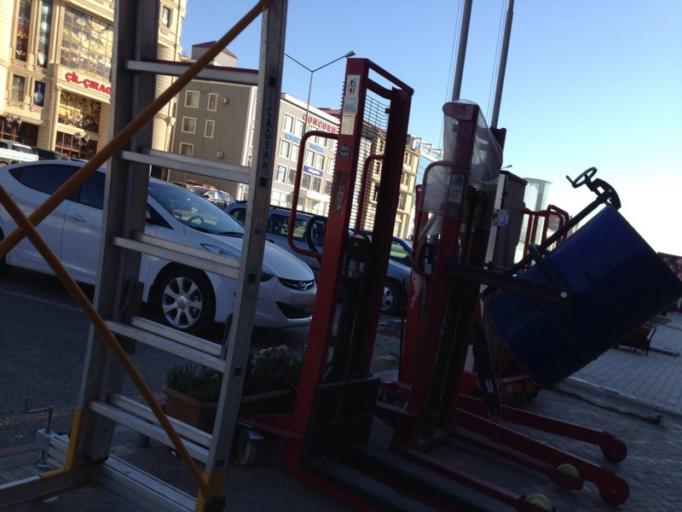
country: AZ
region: Baki
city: Baku
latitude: 40.4108
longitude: 49.8624
